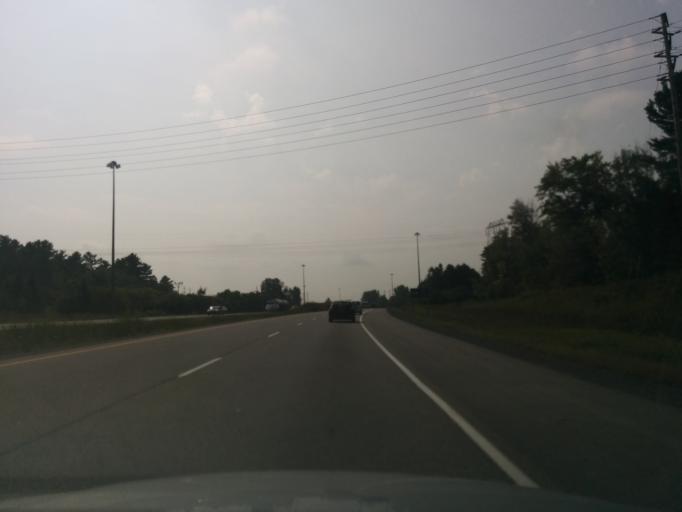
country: CA
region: Ontario
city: Bells Corners
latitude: 45.3238
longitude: -75.8058
